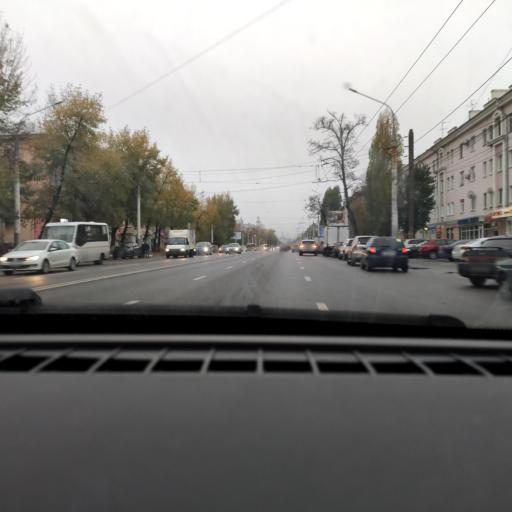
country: RU
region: Voronezj
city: Voronezh
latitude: 51.6391
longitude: 39.2353
